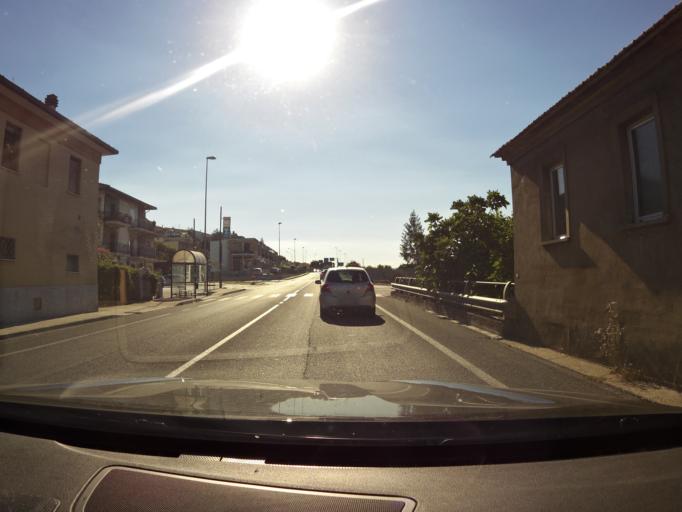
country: IT
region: The Marches
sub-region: Provincia di Ancona
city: Camerano
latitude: 43.4971
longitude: 13.5419
